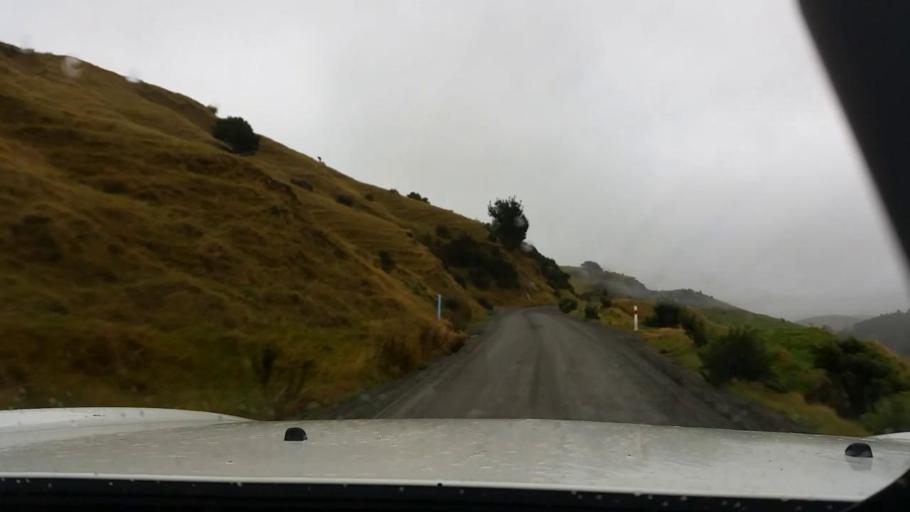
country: NZ
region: Wellington
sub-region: Masterton District
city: Masterton
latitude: -41.2500
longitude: 175.9097
